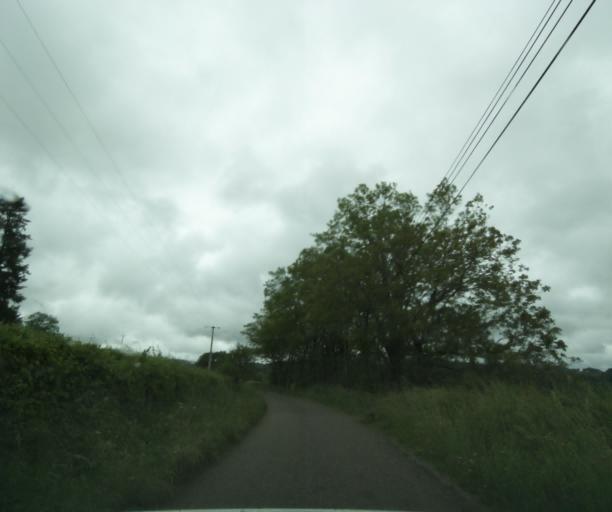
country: FR
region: Bourgogne
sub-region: Departement de Saone-et-Loire
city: Matour
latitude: 46.4579
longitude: 4.4518
